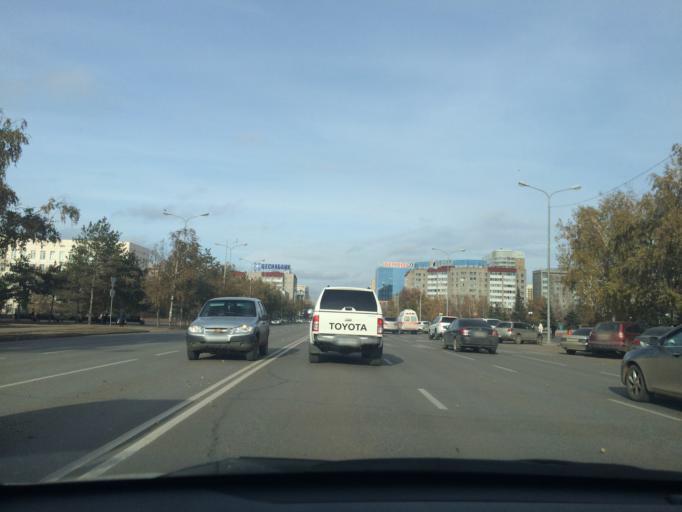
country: KZ
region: Astana Qalasy
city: Astana
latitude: 51.1690
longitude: 71.4264
